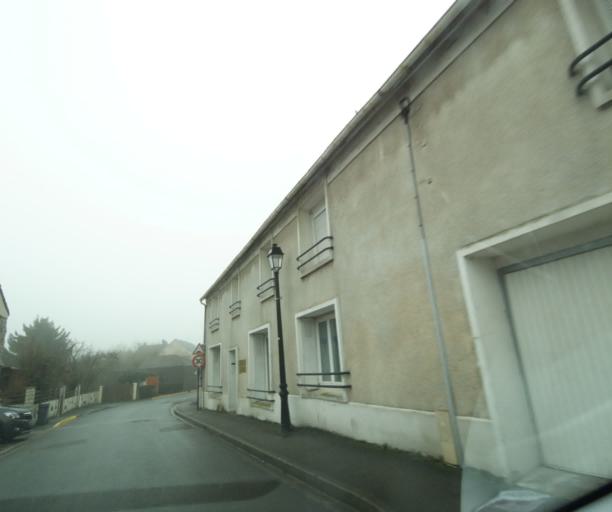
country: FR
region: Ile-de-France
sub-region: Departement de Seine-et-Marne
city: Longperrier
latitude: 49.0504
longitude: 2.6643
